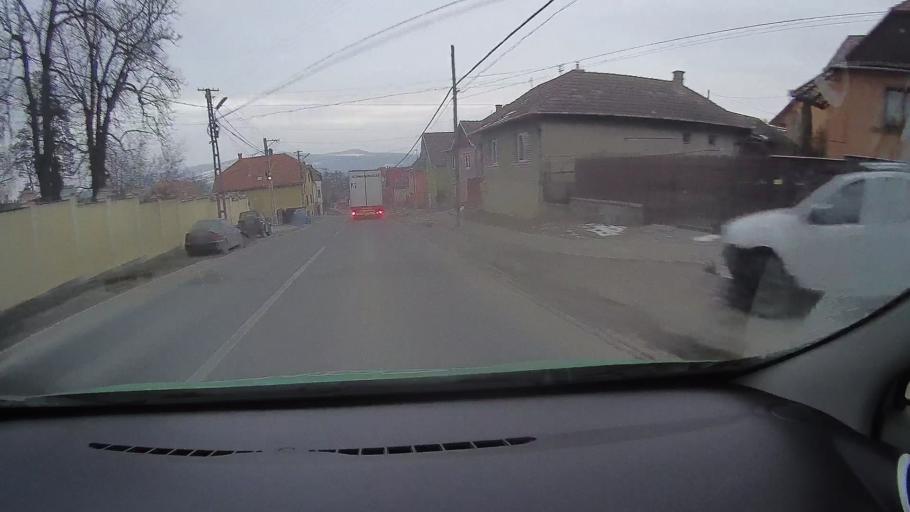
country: RO
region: Harghita
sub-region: Municipiul Odorheiu Secuiesc
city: Odorheiu Secuiesc
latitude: 46.3162
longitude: 25.2818
